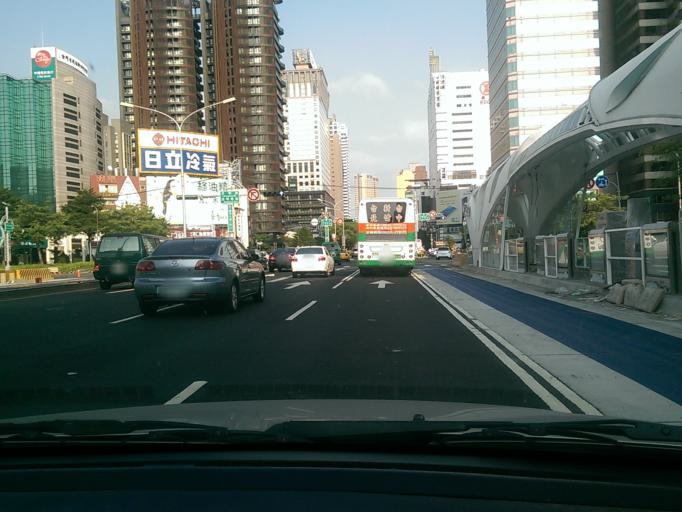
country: TW
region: Taiwan
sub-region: Taichung City
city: Taichung
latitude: 24.1570
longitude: 120.6597
